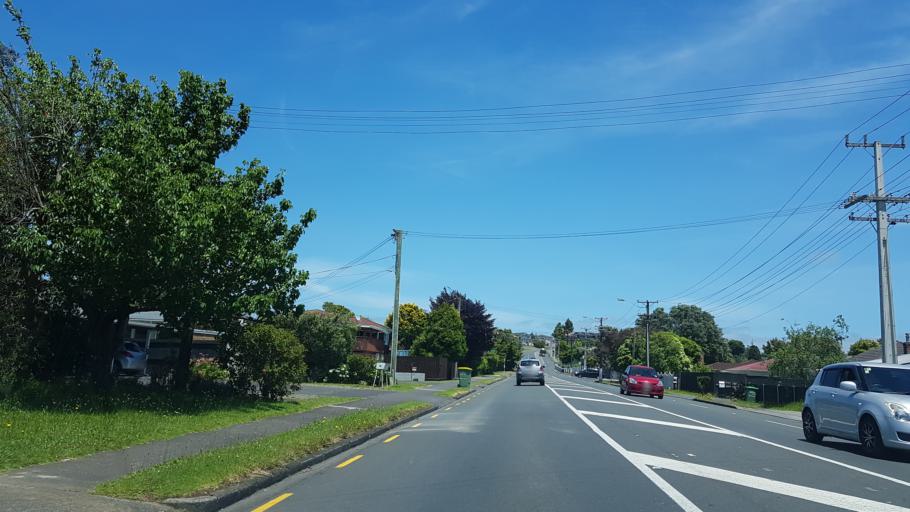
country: NZ
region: Auckland
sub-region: Auckland
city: Waitakere
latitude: -36.9101
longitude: 174.6623
